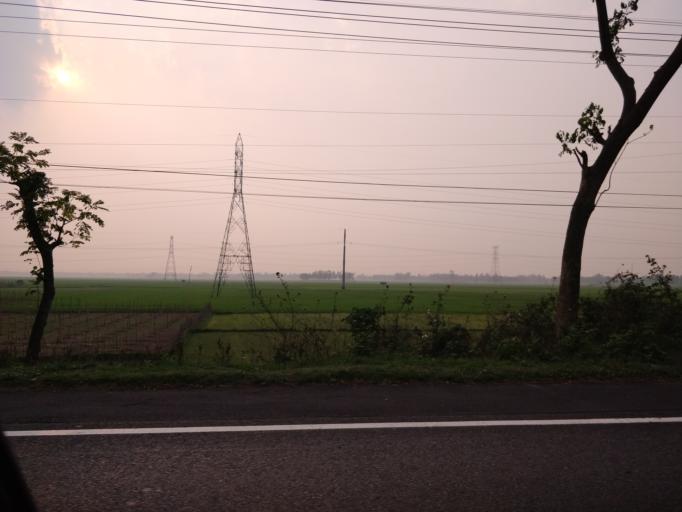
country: BD
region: Sylhet
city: Habiganj
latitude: 24.2039
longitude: 91.3519
